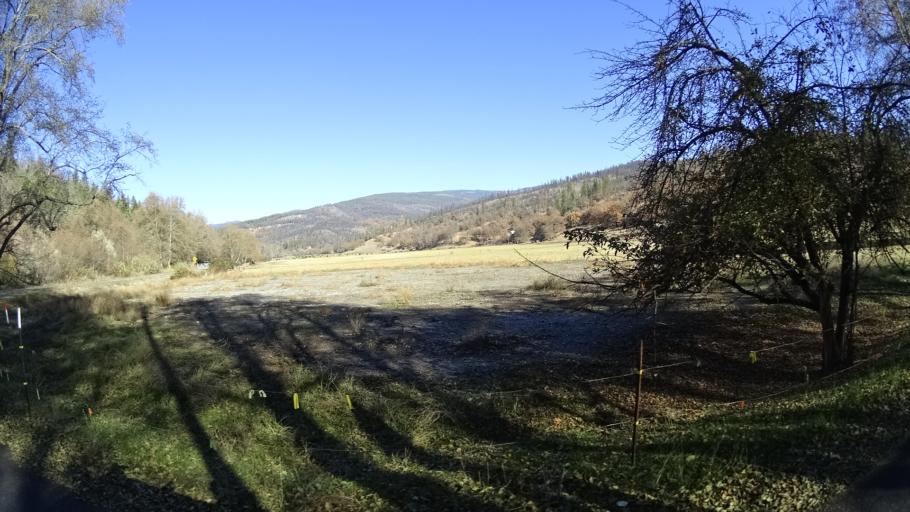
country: US
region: California
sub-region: Siskiyou County
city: Happy Camp
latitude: 41.8247
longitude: -123.0043
